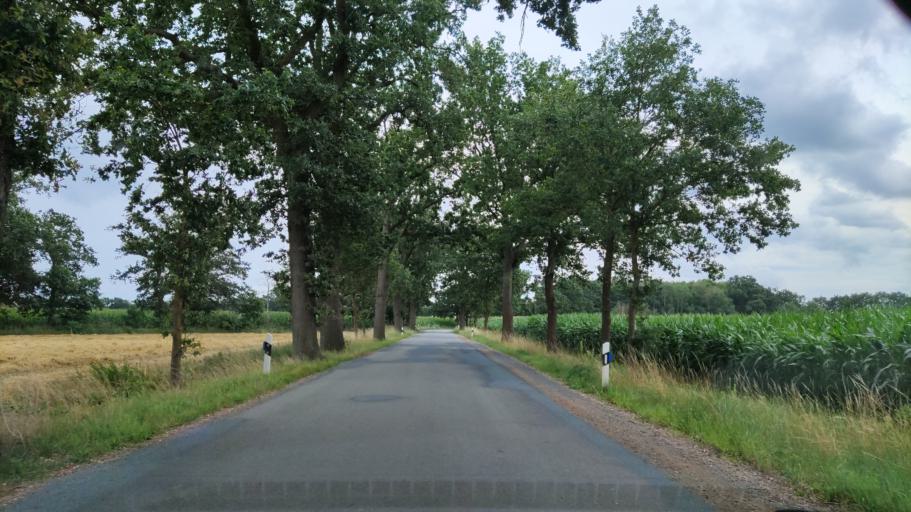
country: DE
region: Lower Saxony
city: Dannenberg
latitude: 53.0678
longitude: 11.1303
